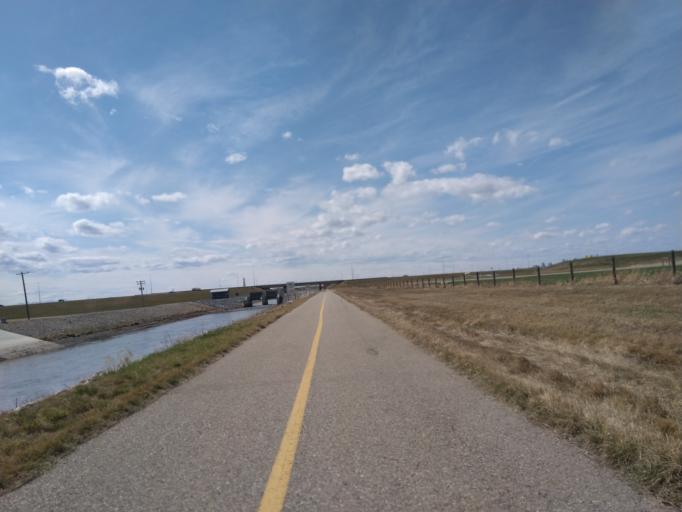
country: CA
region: Alberta
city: Chestermere
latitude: 50.9725
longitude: -113.9128
